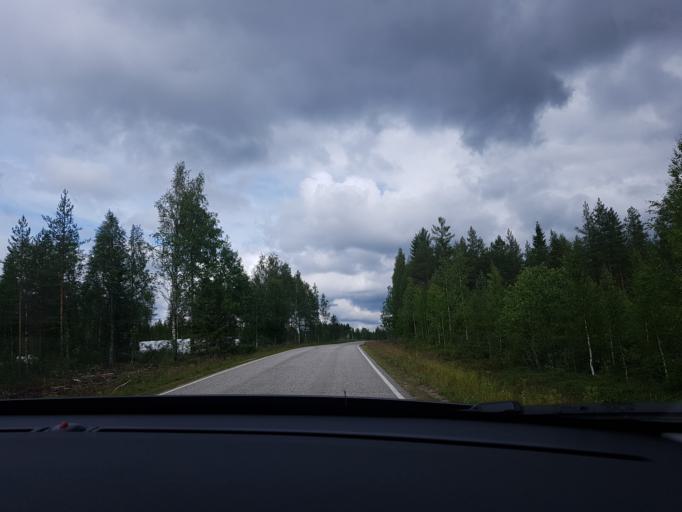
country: FI
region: Kainuu
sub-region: Kehys-Kainuu
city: Kuhmo
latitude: 64.2717
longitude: 29.3755
